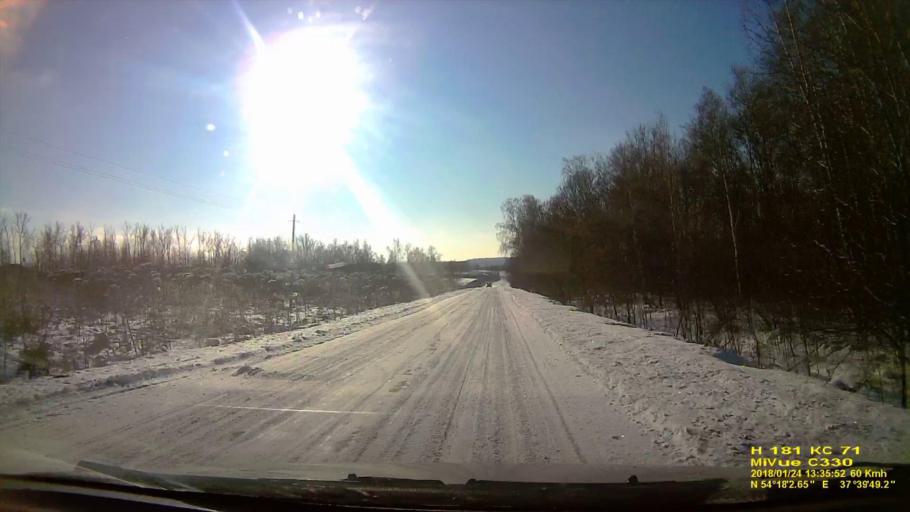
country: RU
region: Tula
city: Revyakino
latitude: 54.3006
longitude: 37.6635
